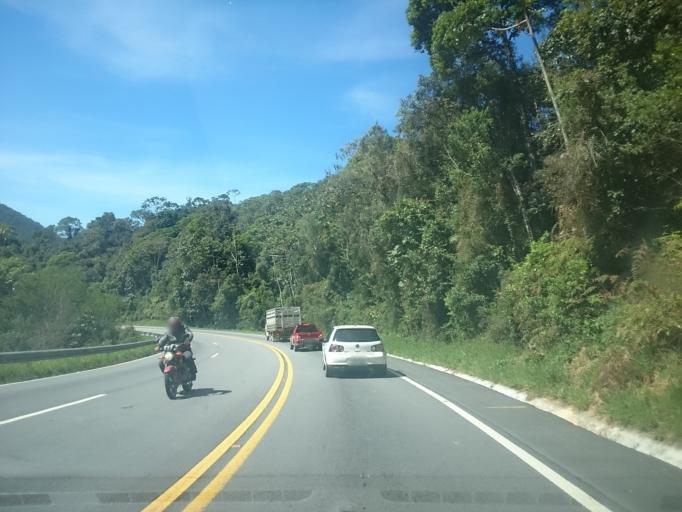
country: BR
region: Santa Catarina
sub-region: Santo Amaro Da Imperatriz
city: Santo Amaro da Imperatriz
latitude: -27.7161
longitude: -48.9418
